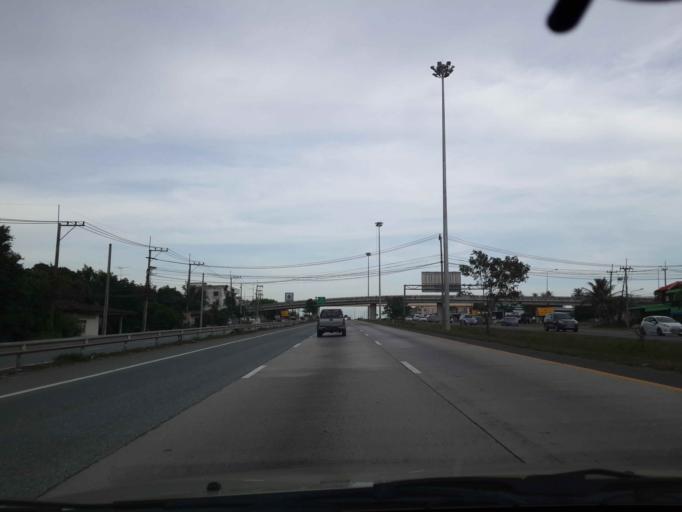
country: TH
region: Chon Buri
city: Phatthaya
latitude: 12.9545
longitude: 100.9872
